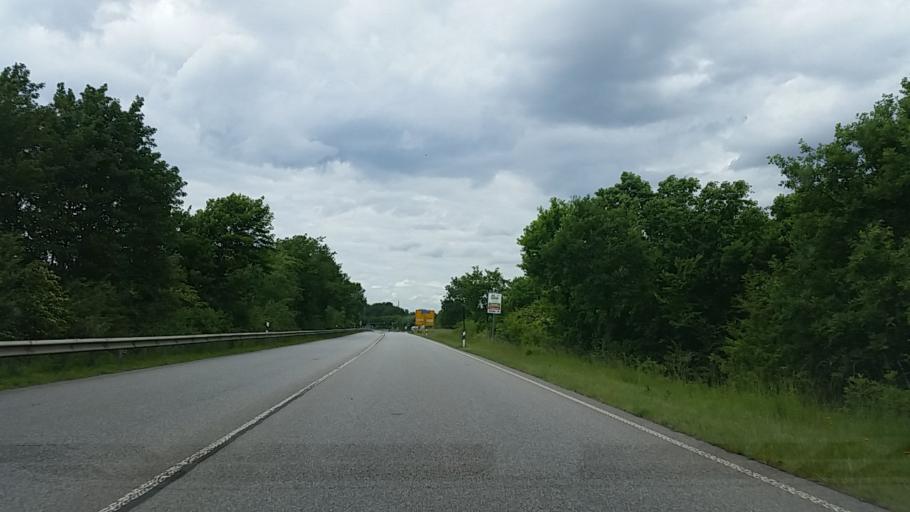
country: DE
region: Schleswig-Holstein
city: Glinde
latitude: 53.5643
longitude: 10.2245
